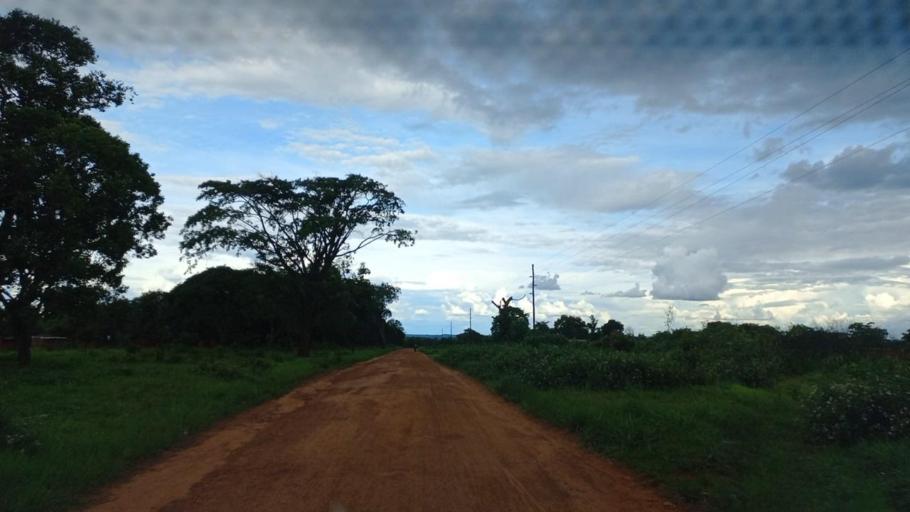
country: ZM
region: North-Western
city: Mwinilunga
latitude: -11.7753
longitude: 24.3888
